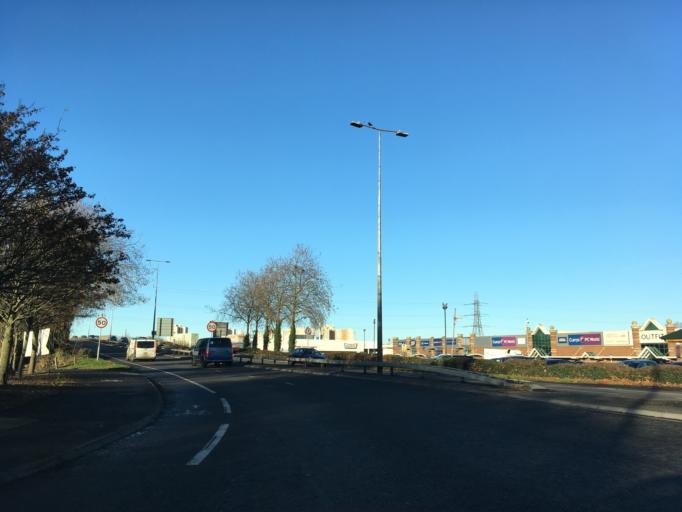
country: GB
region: England
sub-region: Bristol
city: Bristol
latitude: 51.4465
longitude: -2.5610
